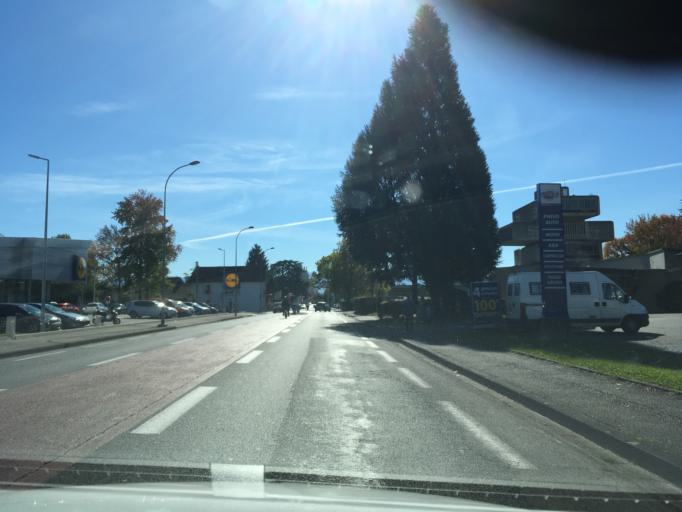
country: FR
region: Aquitaine
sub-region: Departement des Pyrenees-Atlantiques
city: Lons
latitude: 43.3215
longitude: -0.3793
